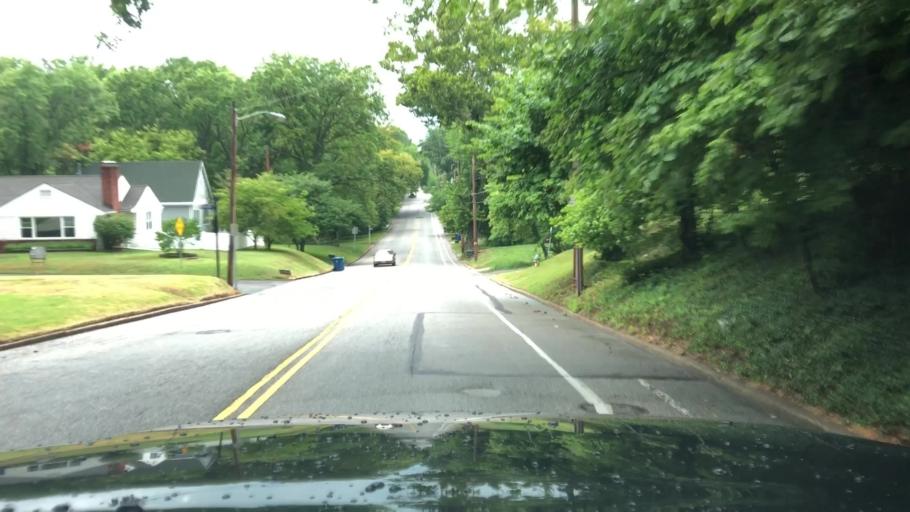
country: US
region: Missouri
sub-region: Saint Charles County
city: Saint Charles
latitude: 38.7912
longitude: -90.4981
